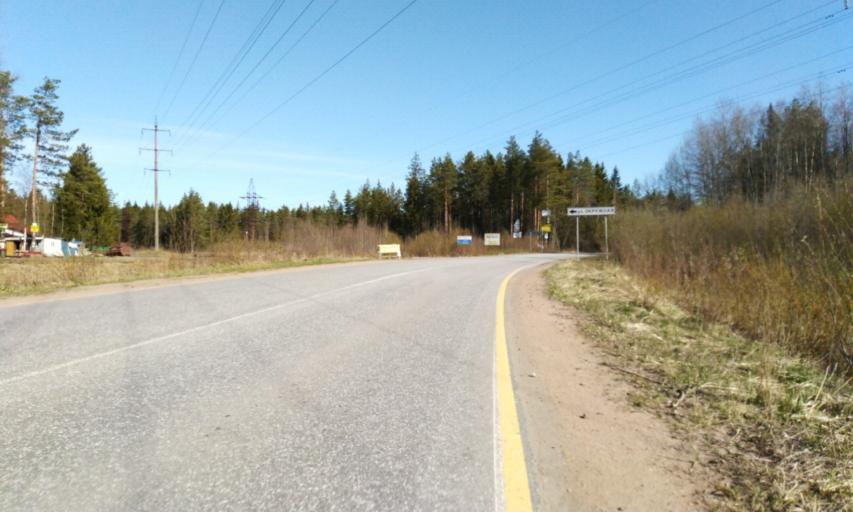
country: RU
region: Leningrad
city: Garbolovo
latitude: 60.3401
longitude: 30.4357
